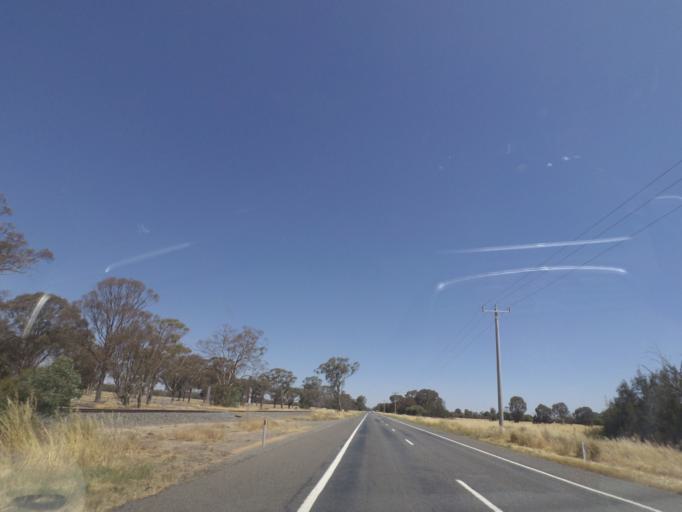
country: AU
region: Victoria
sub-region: Greater Shepparton
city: Shepparton
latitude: -36.2101
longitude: 145.4319
